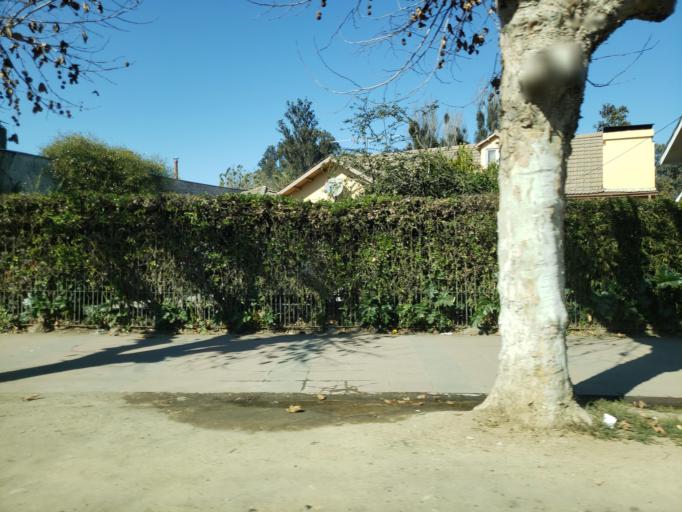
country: CL
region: Santiago Metropolitan
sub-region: Provincia de Talagante
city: El Monte
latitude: -33.6805
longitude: -70.9805
